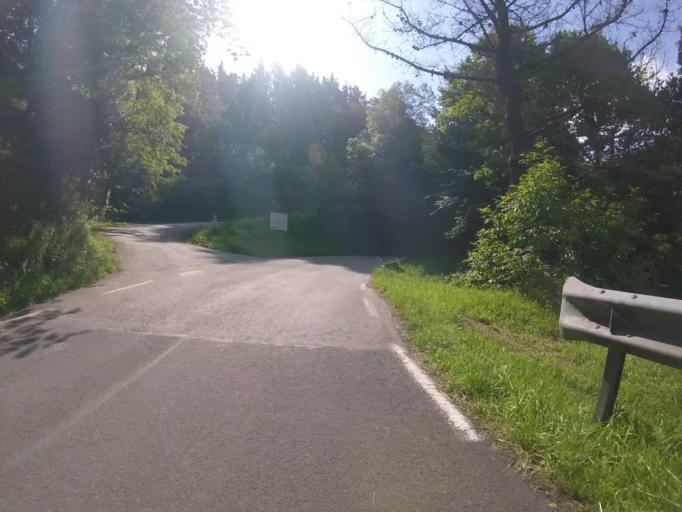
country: ES
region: Basque Country
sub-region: Provincia de Guipuzcoa
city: Alquiza
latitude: 43.1665
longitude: -2.0952
